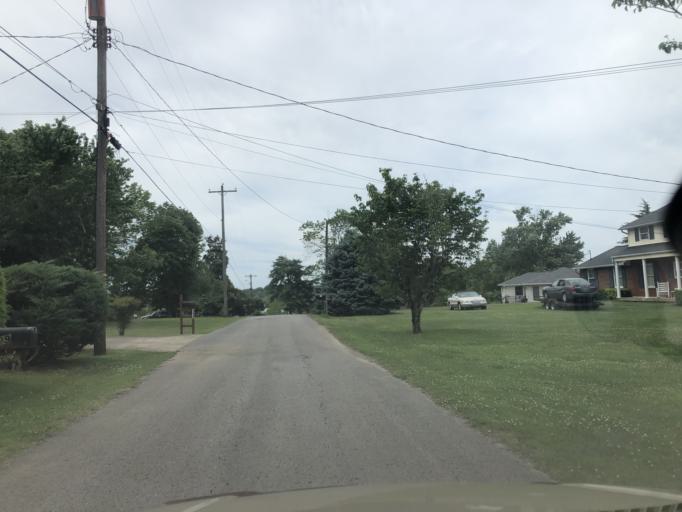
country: US
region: Tennessee
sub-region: Davidson County
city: Lakewood
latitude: 36.2530
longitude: -86.6173
